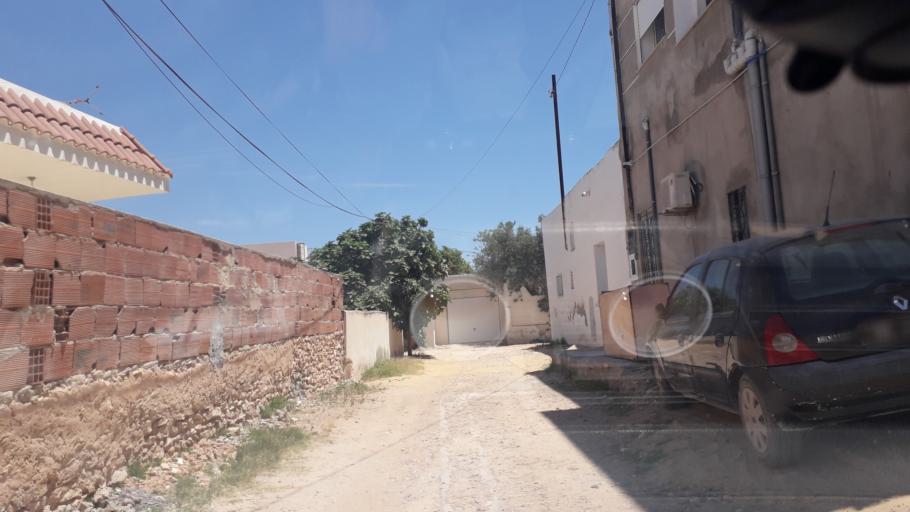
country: TN
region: Safaqis
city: Al Qarmadah
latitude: 34.8148
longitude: 10.7653
